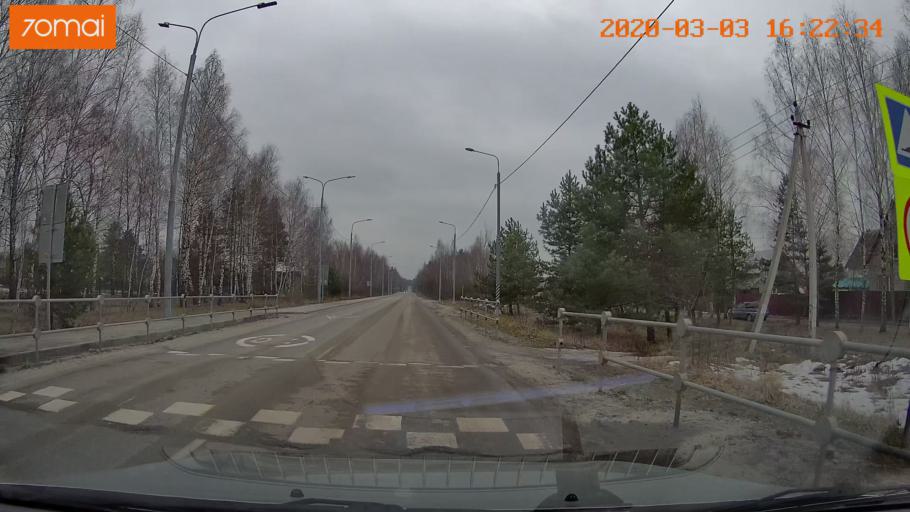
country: RU
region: Moskovskaya
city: Imeni Tsyurupy
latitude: 55.4910
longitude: 38.6484
